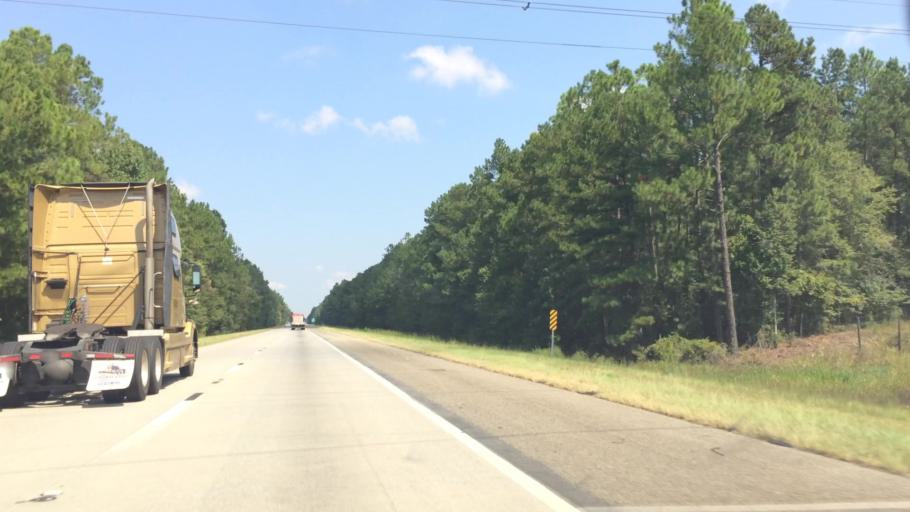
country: US
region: South Carolina
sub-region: Dorchester County
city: Saint George
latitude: 33.0600
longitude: -80.6635
